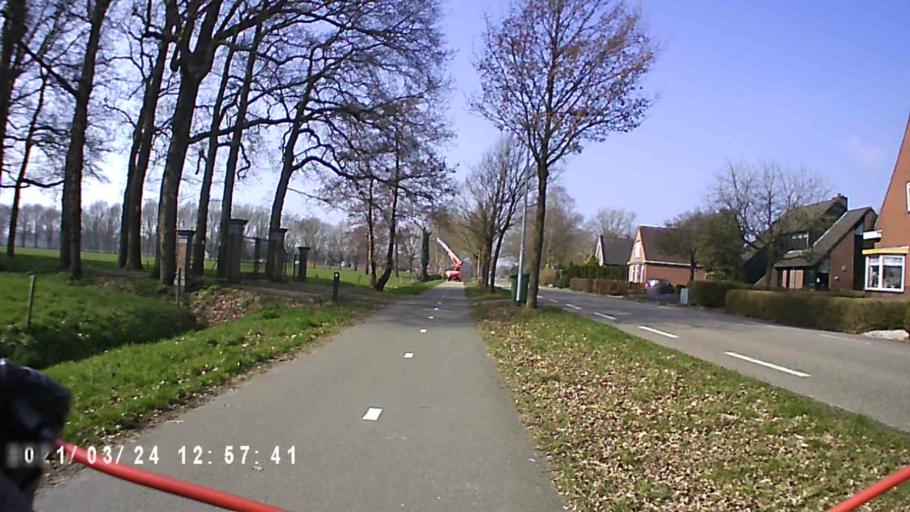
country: NL
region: Groningen
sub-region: Gemeente Grootegast
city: Grootegast
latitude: 53.1512
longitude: 6.3006
